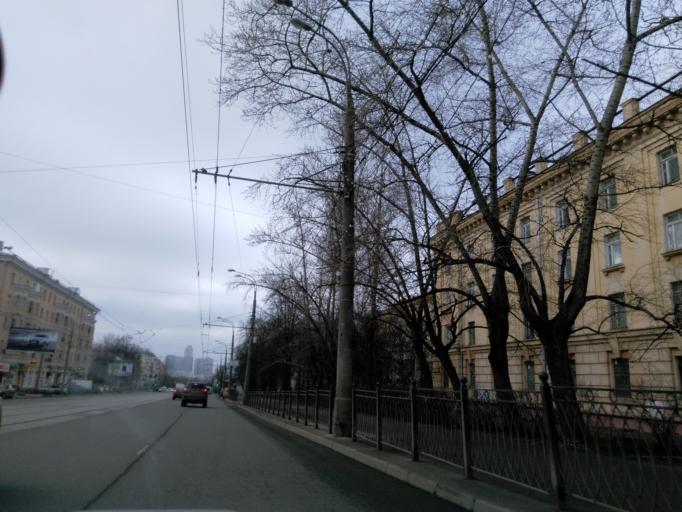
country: RU
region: Moscow
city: Pokrovskoye-Streshnevo
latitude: 55.8346
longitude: 37.4538
